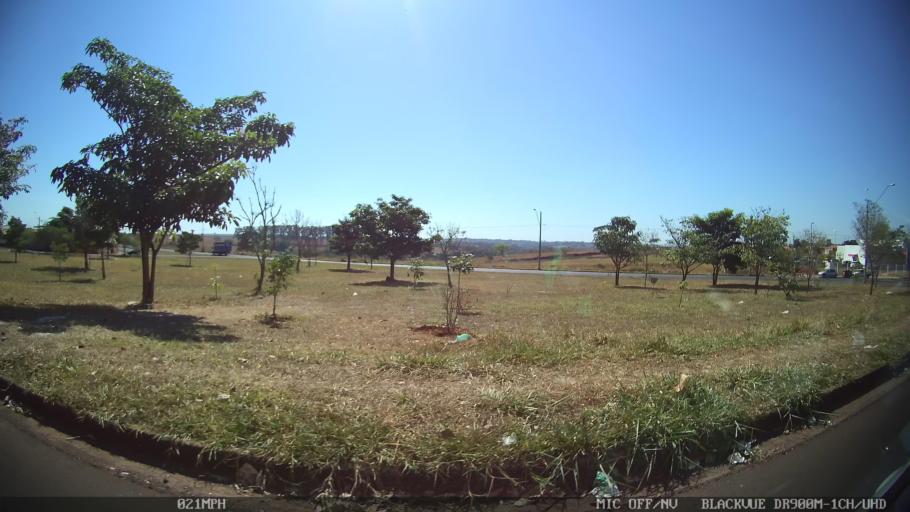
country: BR
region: Sao Paulo
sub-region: Sao Jose Do Rio Preto
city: Sao Jose do Rio Preto
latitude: -20.7409
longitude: -49.4107
